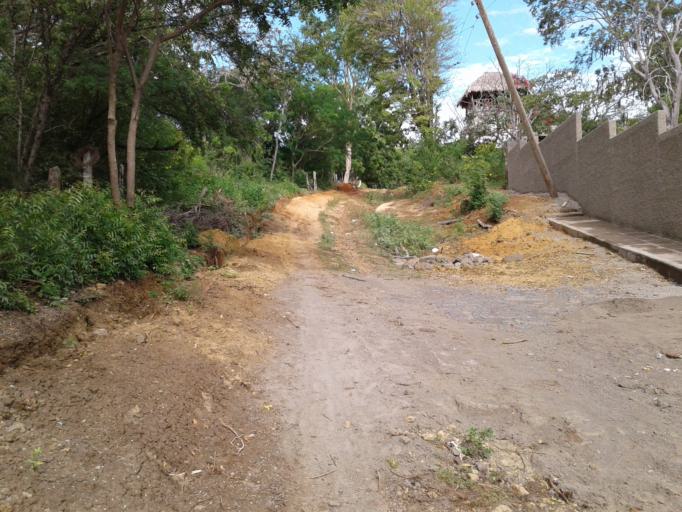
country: NI
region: Carazo
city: El Rosario
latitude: 11.6289
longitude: -86.3394
